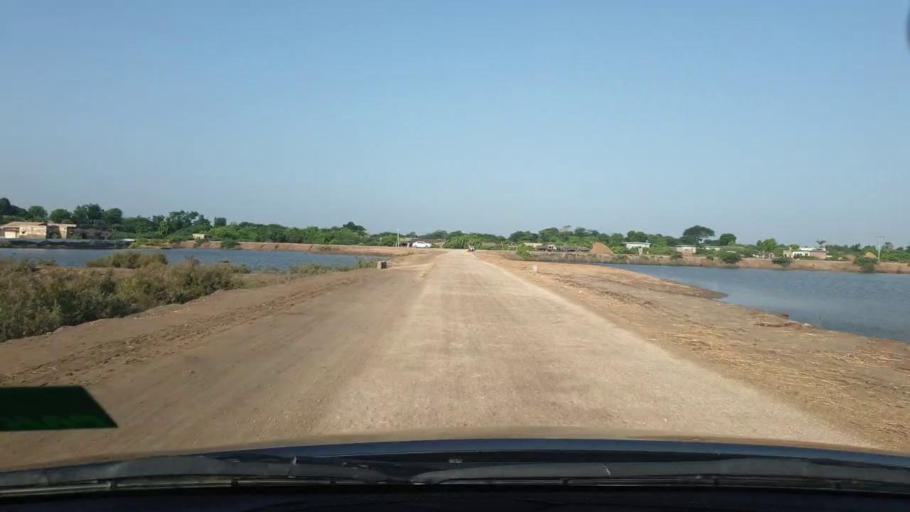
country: PK
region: Sindh
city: Tando Bago
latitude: 24.7225
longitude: 68.9438
